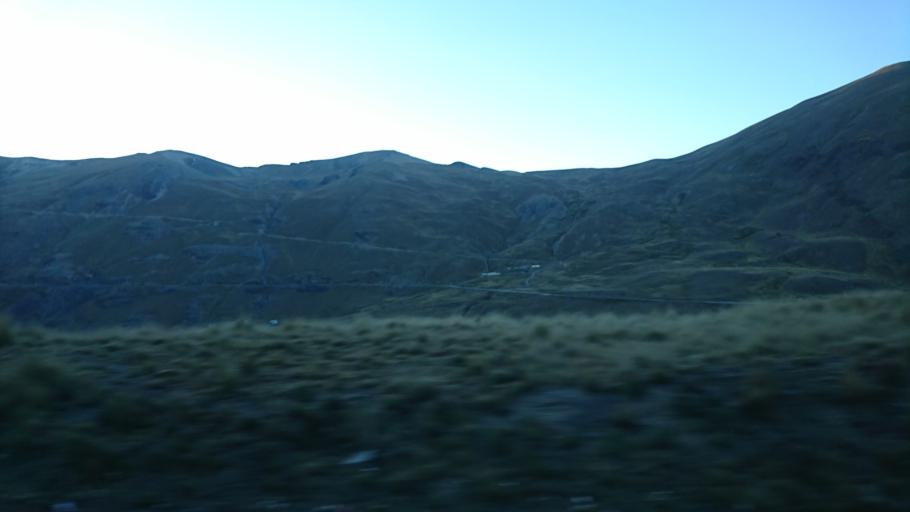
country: BO
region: La Paz
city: La Paz
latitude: -16.3985
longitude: -68.0453
